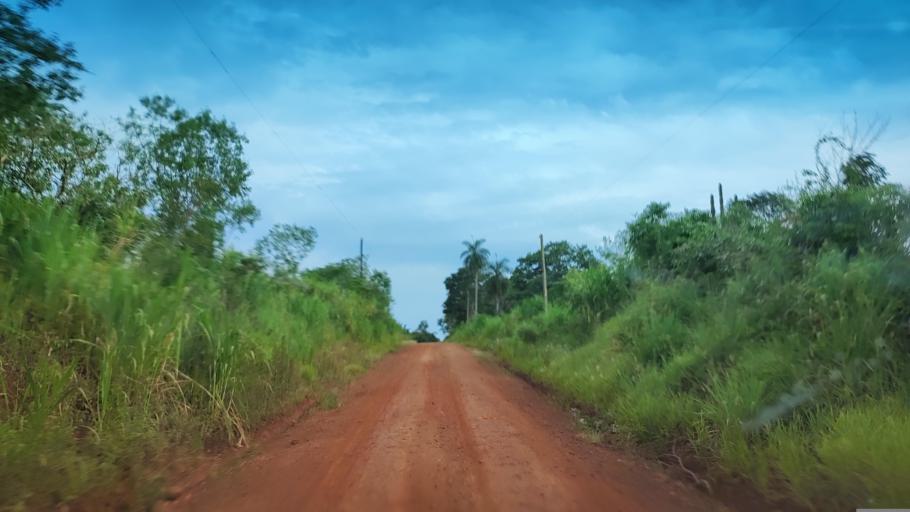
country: AR
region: Misiones
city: Gobernador Roca
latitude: -27.1625
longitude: -55.4587
